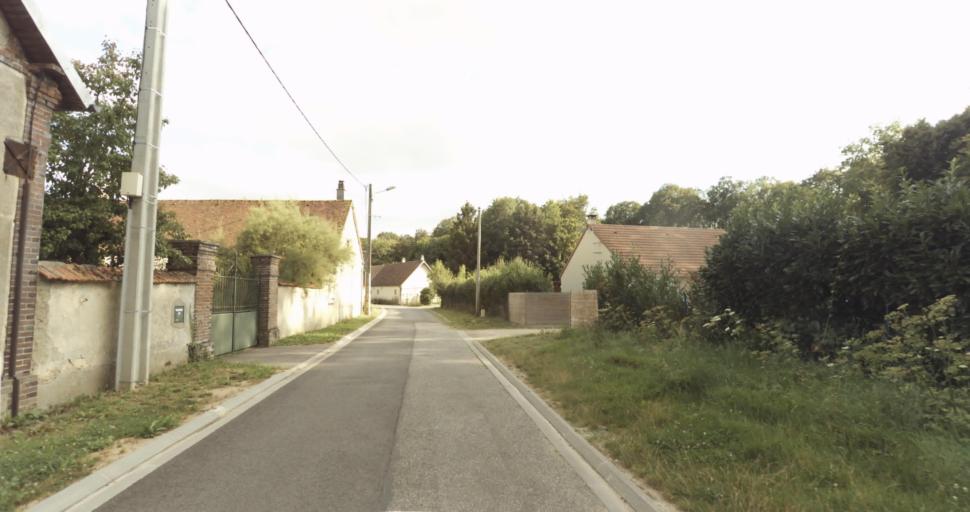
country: FR
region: Haute-Normandie
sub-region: Departement de l'Eure
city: La Couture-Boussey
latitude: 48.8894
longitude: 1.3787
